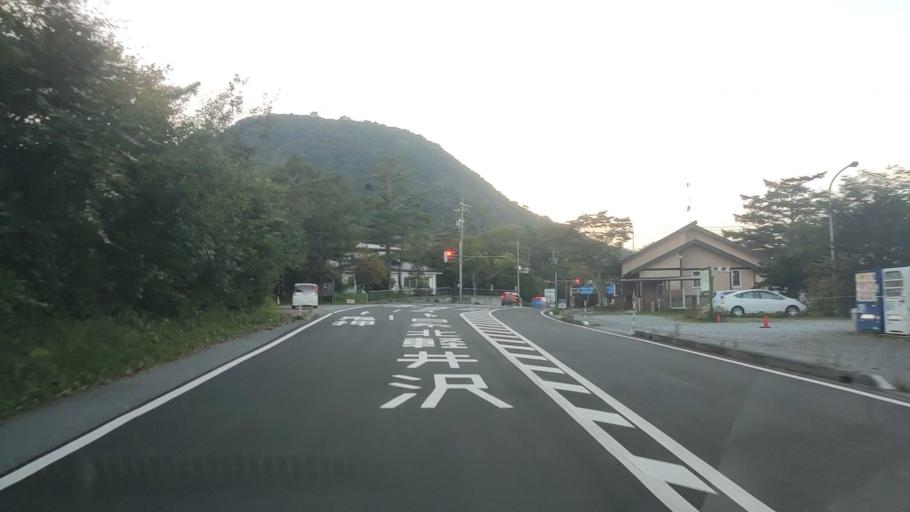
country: JP
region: Nagano
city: Komoro
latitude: 36.4038
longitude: 138.5698
